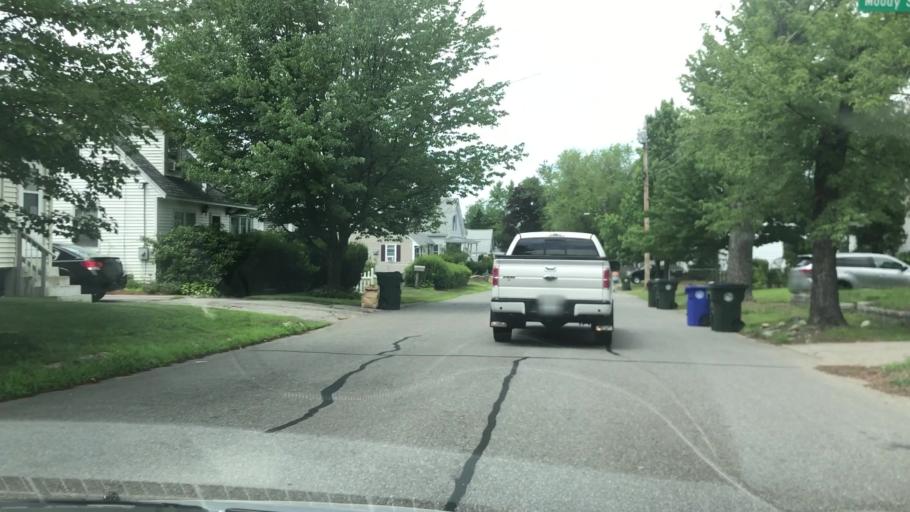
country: US
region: New Hampshire
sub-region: Hillsborough County
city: Manchester
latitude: 42.9741
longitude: -71.4326
